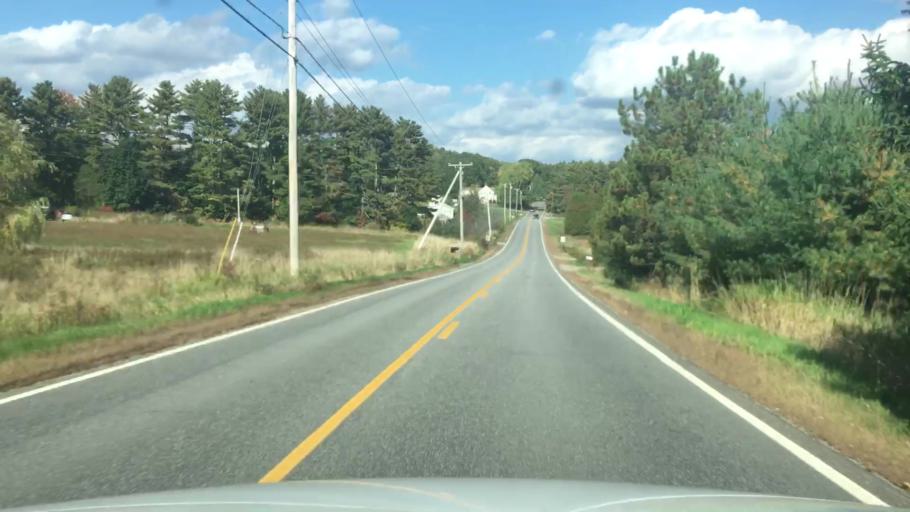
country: US
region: Maine
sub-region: Knox County
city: Union
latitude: 44.2282
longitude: -69.2835
